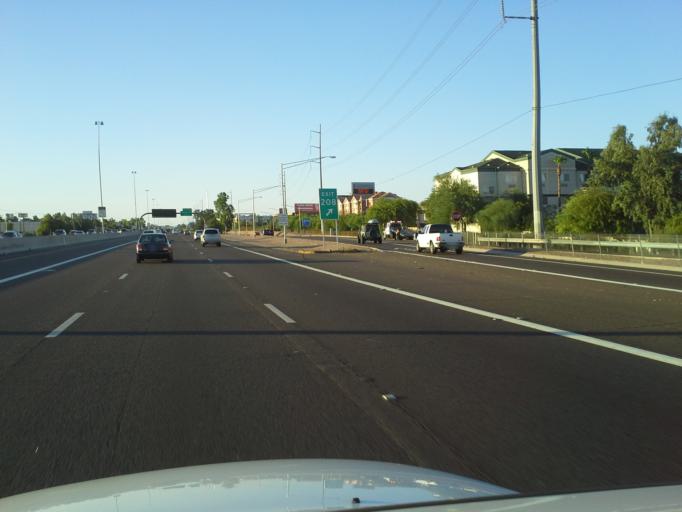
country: US
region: Arizona
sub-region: Maricopa County
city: Glendale
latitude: 33.5782
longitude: -112.1168
